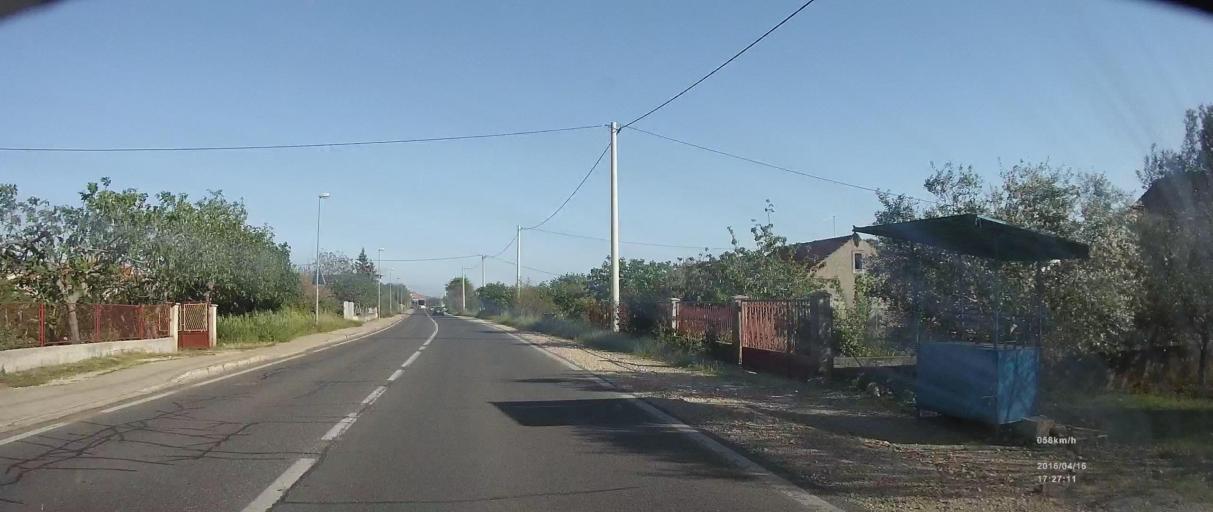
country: HR
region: Zadarska
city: Sukosan
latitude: 44.0437
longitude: 15.3176
